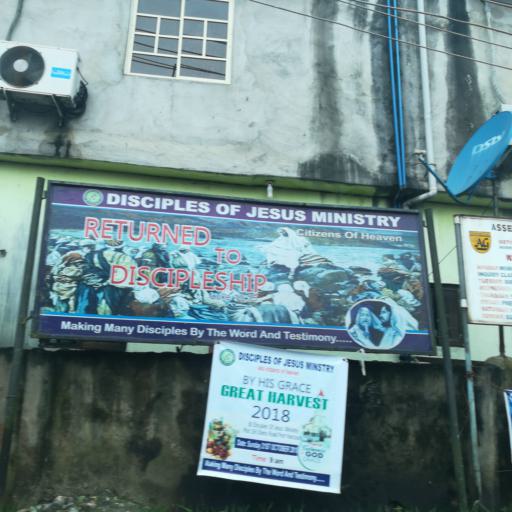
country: NG
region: Rivers
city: Port Harcourt
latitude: 4.7509
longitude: 7.0087
